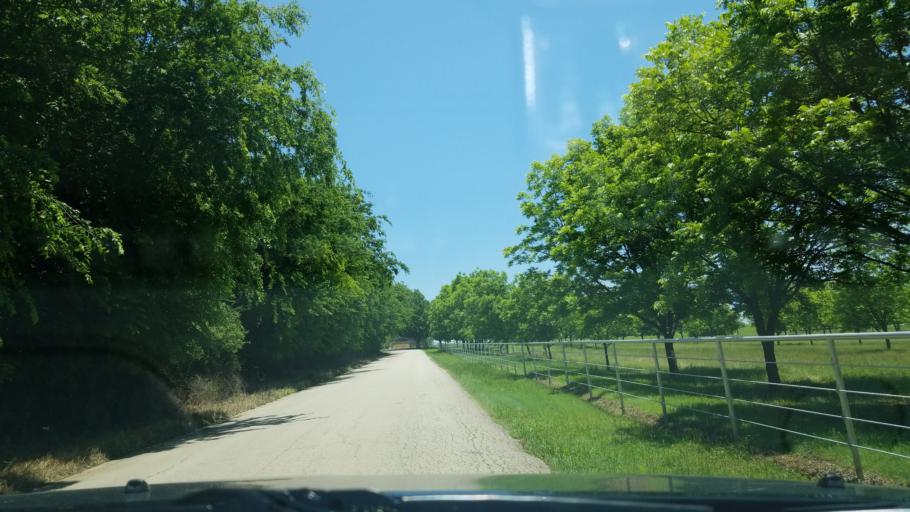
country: US
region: Texas
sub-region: Denton County
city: Sanger
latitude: 33.3512
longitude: -97.1979
